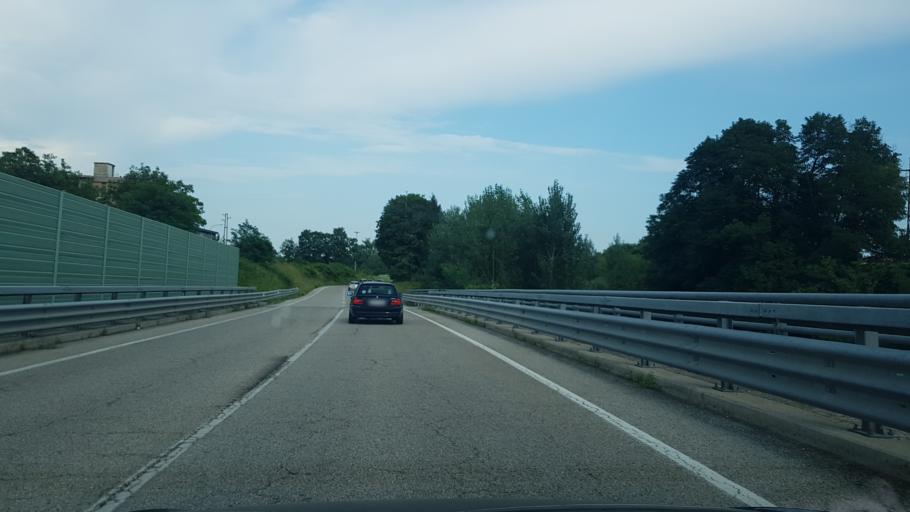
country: IT
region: Veneto
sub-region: Provincia di Vicenza
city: Torrebelvicino
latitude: 45.7137
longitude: 11.3287
